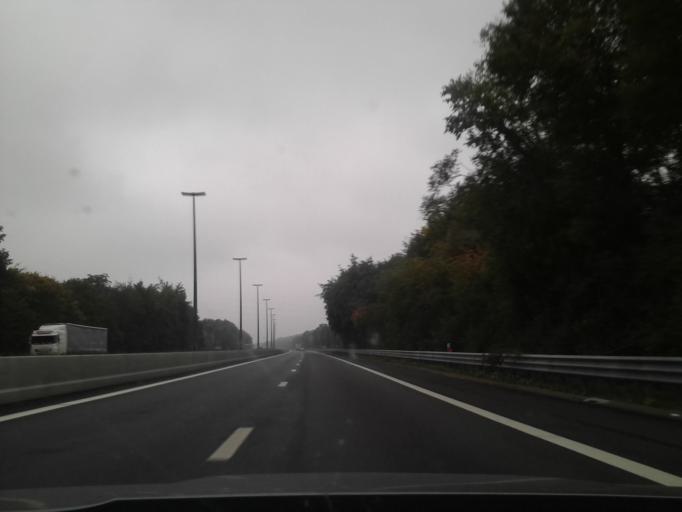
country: BE
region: Wallonia
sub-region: Province du Hainaut
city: Hensies
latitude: 50.4509
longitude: 3.7278
